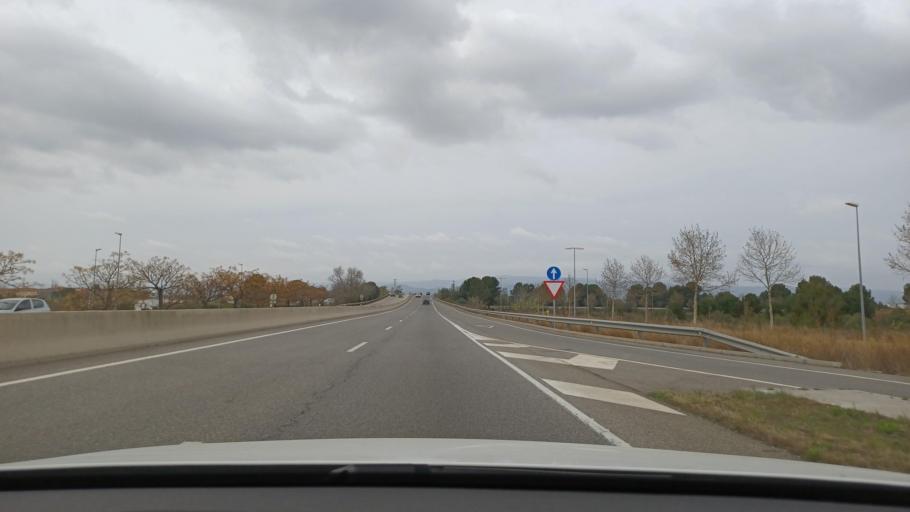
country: ES
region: Catalonia
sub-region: Provincia de Tarragona
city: Vila-seca
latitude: 41.1235
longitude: 1.1561
